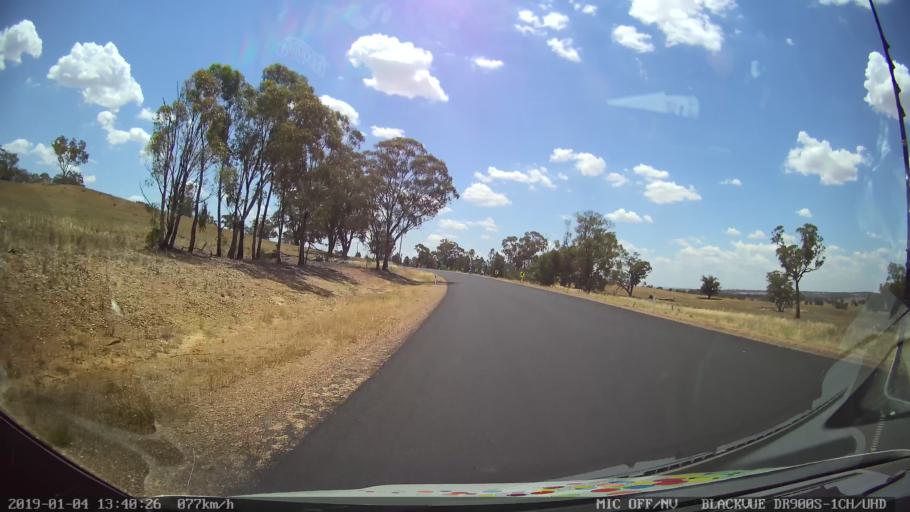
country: AU
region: New South Wales
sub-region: Dubbo Municipality
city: Dubbo
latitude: -32.5143
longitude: 148.5552
